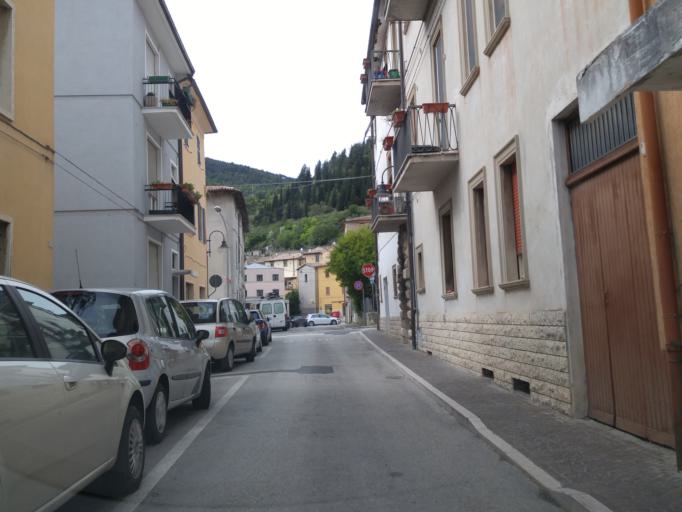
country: IT
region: The Marches
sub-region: Provincia di Pesaro e Urbino
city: Fossombrone
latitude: 43.6876
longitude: 12.8082
